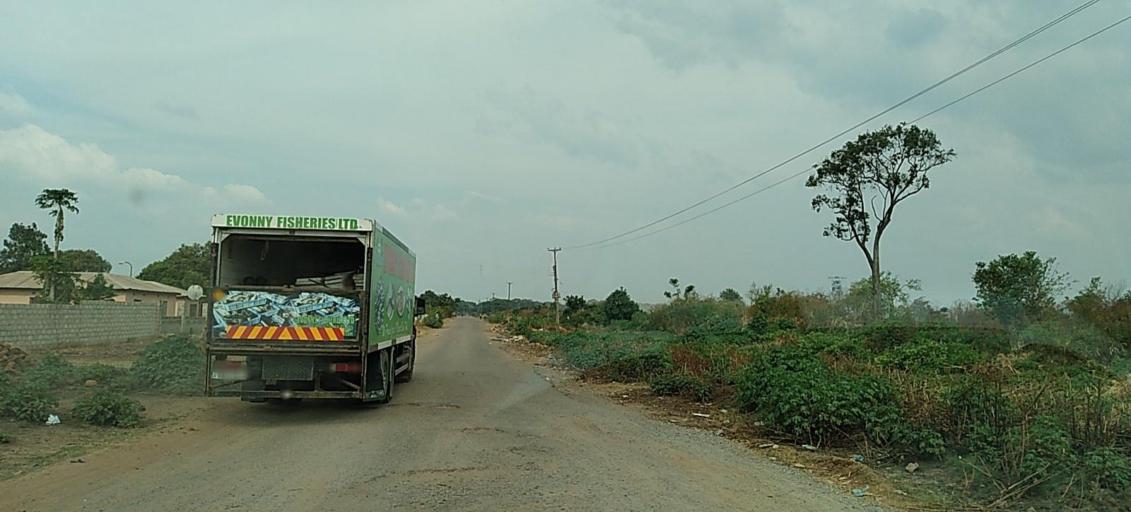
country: ZM
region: Copperbelt
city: Chililabombwe
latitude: -12.3731
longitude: 27.8167
